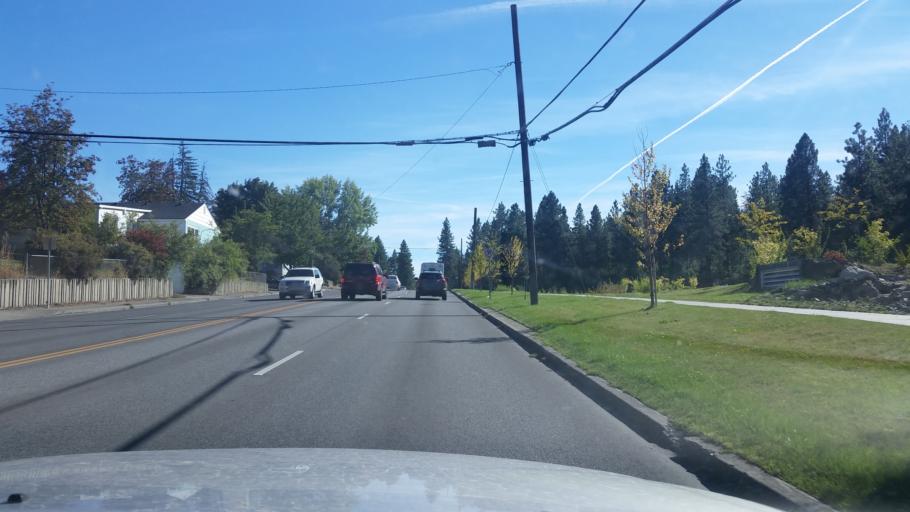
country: US
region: Washington
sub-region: Spokane County
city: Spokane
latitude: 47.6371
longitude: -117.3632
